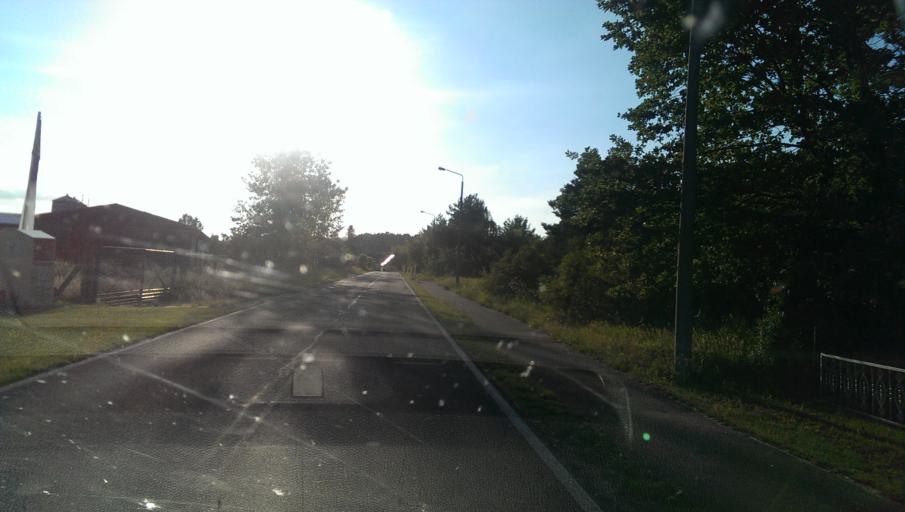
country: DE
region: Brandenburg
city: Trebbin
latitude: 52.2392
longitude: 13.1721
